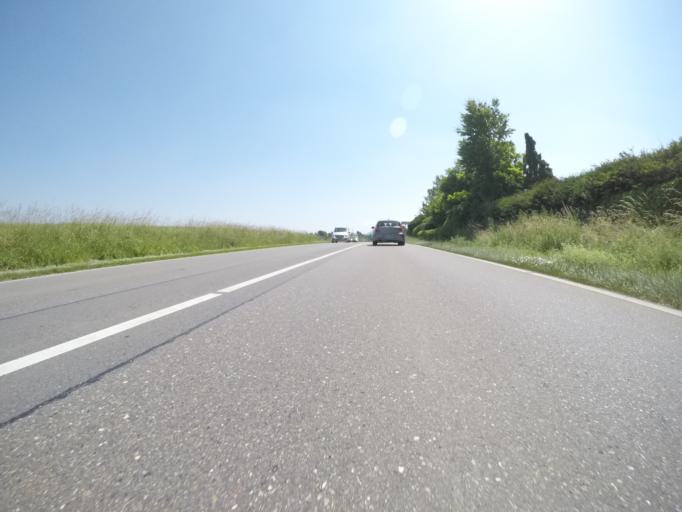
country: DE
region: Baden-Wuerttemberg
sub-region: Regierungsbezirk Stuttgart
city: Dettingen unter Teck
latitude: 48.6176
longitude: 9.4645
